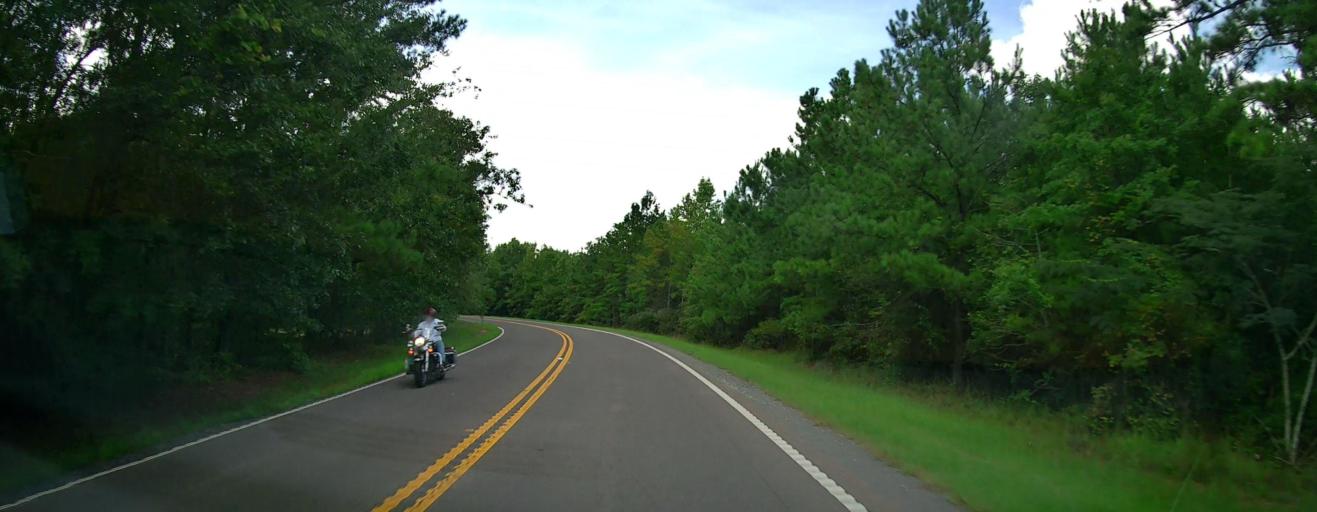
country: US
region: Georgia
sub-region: Talbot County
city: Talbotton
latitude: 32.6318
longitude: -84.4892
